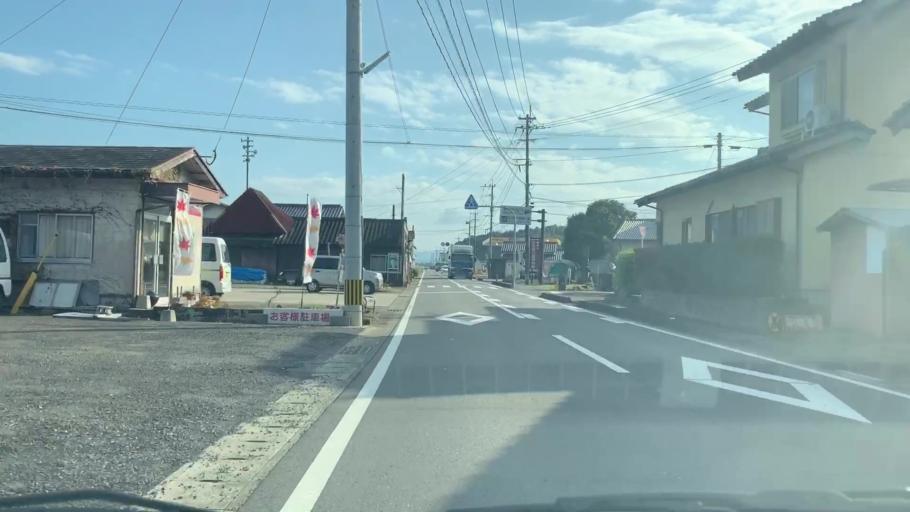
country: JP
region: Saga Prefecture
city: Takeocho-takeo
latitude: 33.1570
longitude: 130.0629
